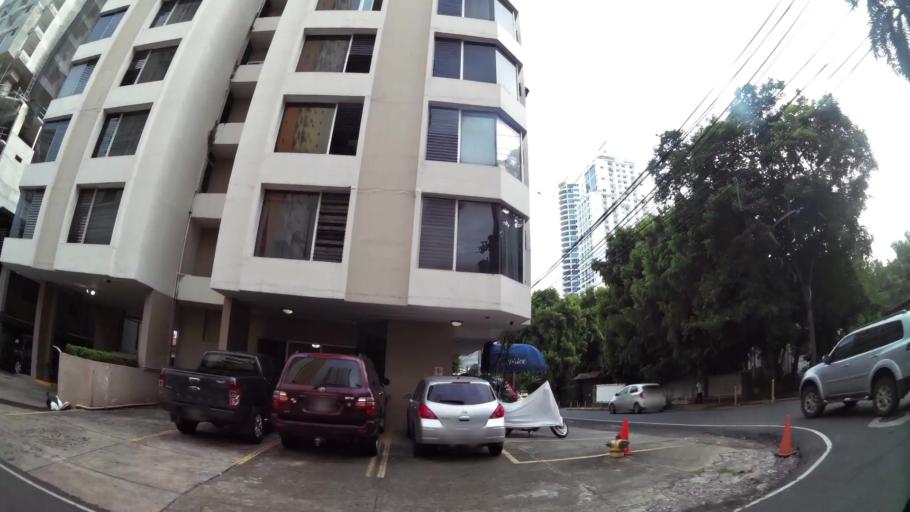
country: PA
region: Panama
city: Panama
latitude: 8.9938
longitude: -79.5056
